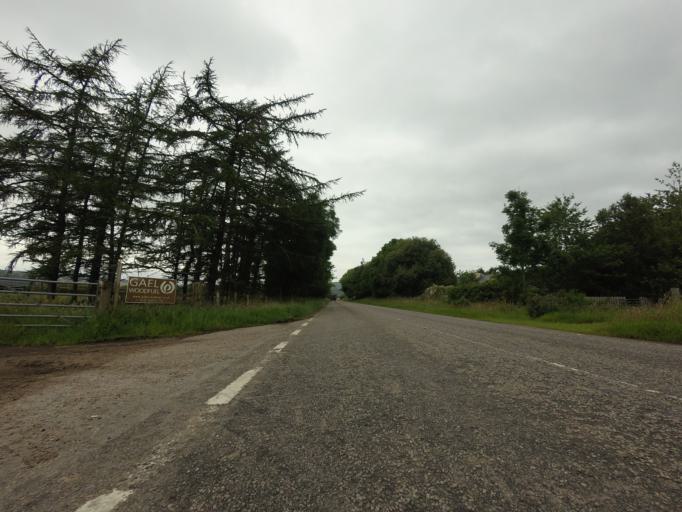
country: GB
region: Scotland
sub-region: Highland
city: Alness
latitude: 57.9141
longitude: -4.3829
